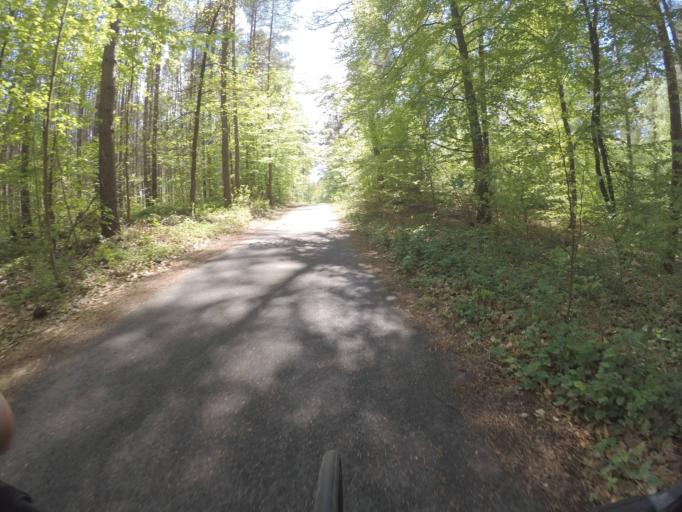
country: DE
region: Brandenburg
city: Rudnitz
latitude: 52.7379
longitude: 13.6121
